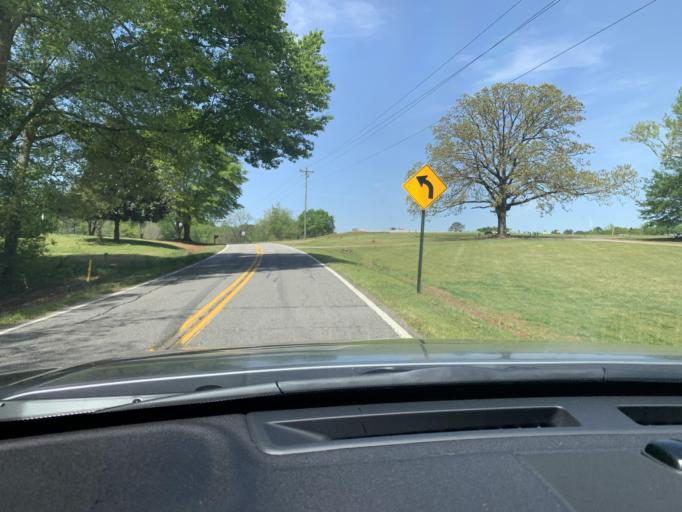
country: US
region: Georgia
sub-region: Barrow County
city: Statham
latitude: 33.9035
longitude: -83.6306
